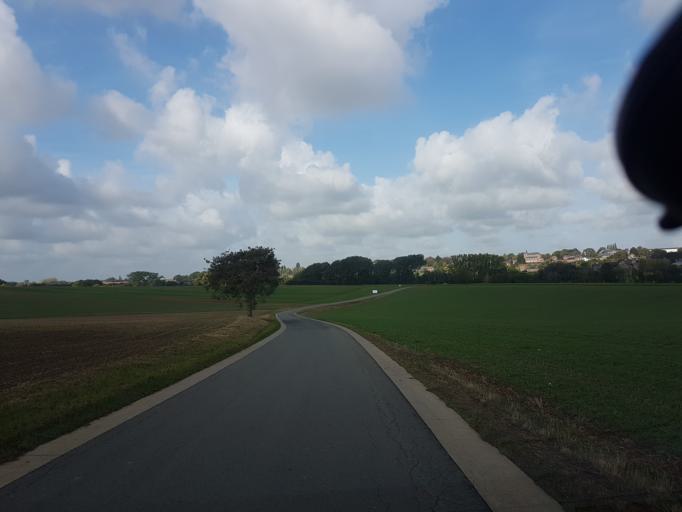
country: BE
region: Wallonia
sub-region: Province de Liege
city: Heron
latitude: 50.5435
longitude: 5.1085
